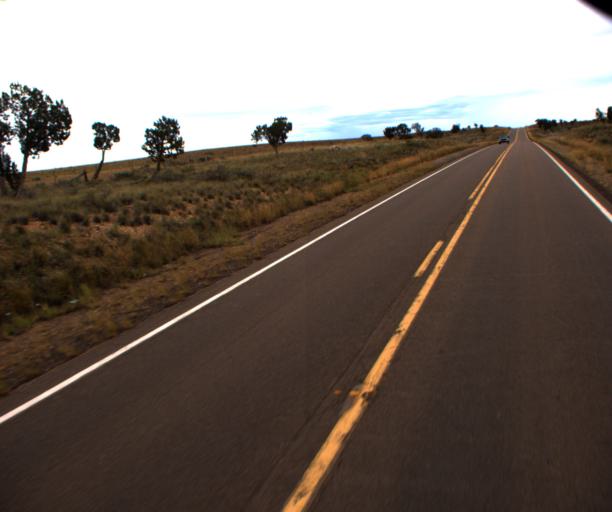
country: US
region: Arizona
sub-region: Navajo County
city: Snowflake
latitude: 34.6099
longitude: -110.0901
